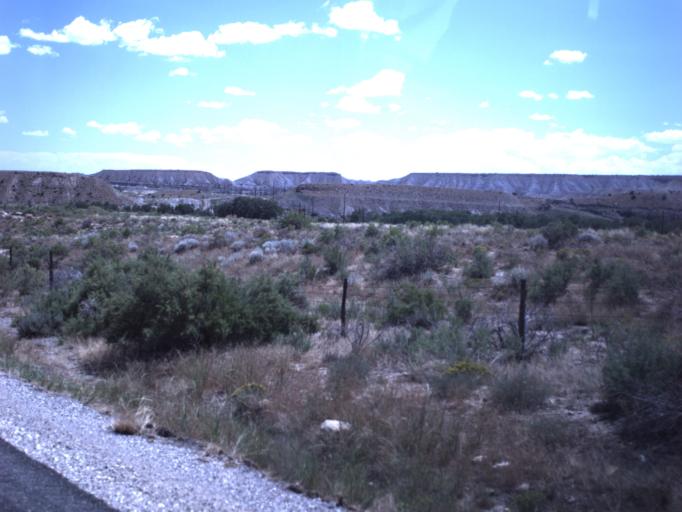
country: US
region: Utah
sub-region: Emery County
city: Orangeville
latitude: 39.2538
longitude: -111.0964
